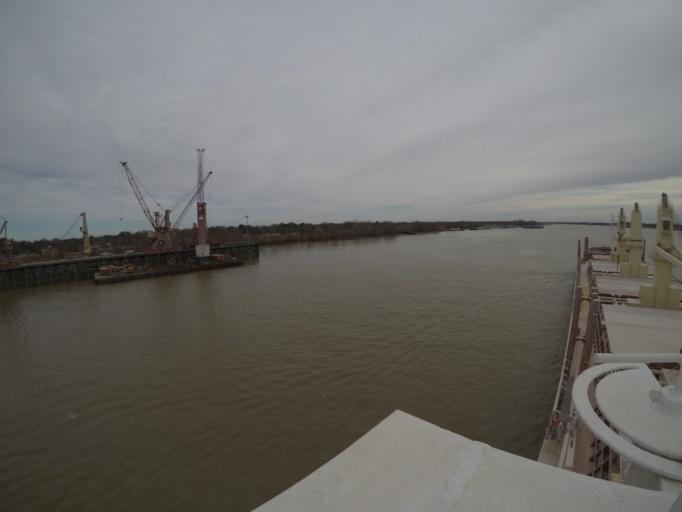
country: US
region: Louisiana
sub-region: Saint John the Baptist Parish
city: Edgard
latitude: 30.0518
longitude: -90.5630
